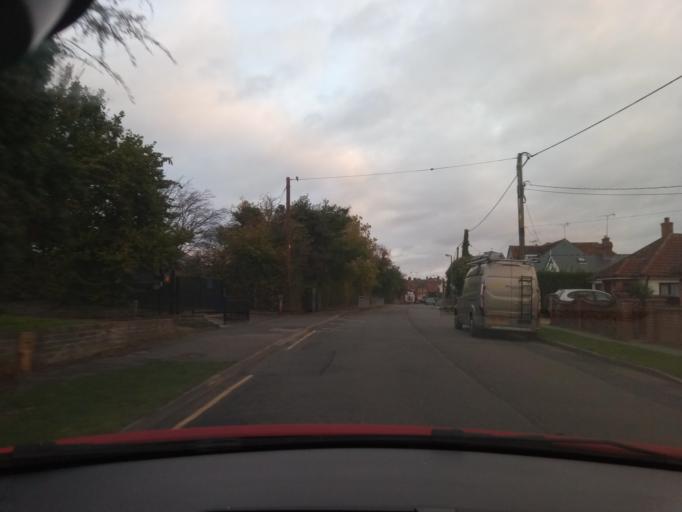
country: GB
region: England
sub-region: Essex
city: West Mersea
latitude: 51.7764
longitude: 0.9187
